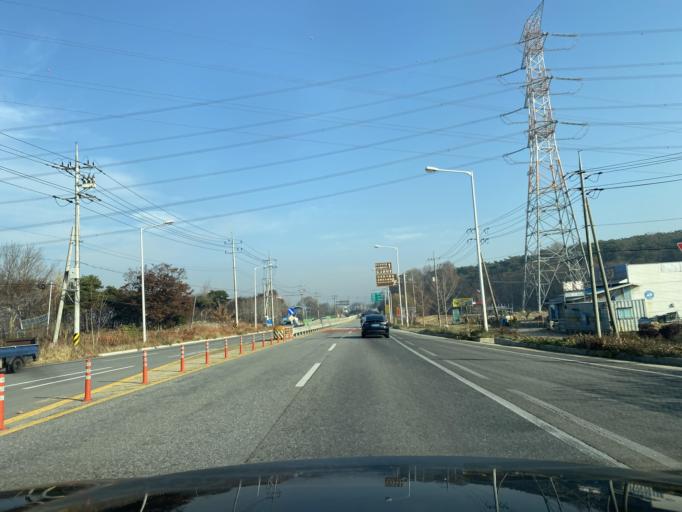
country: KR
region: Chungcheongnam-do
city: Yesan
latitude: 36.7407
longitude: 126.8596
